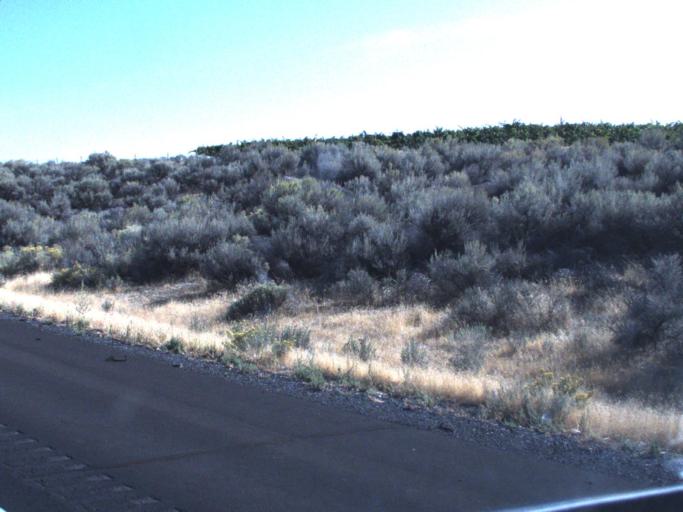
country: US
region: Washington
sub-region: Benton County
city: West Richland
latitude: 46.2600
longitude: -119.3906
